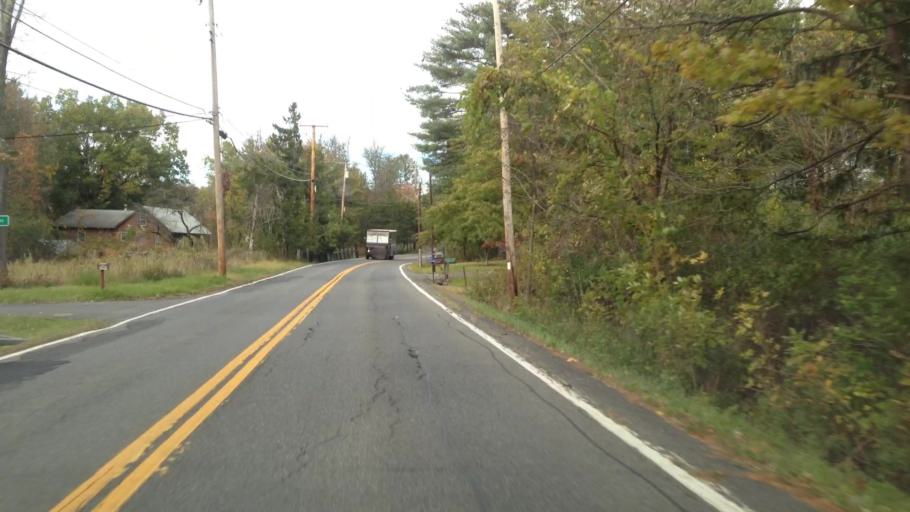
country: US
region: New York
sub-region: Ulster County
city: Tillson
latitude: 41.8447
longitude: -74.0381
